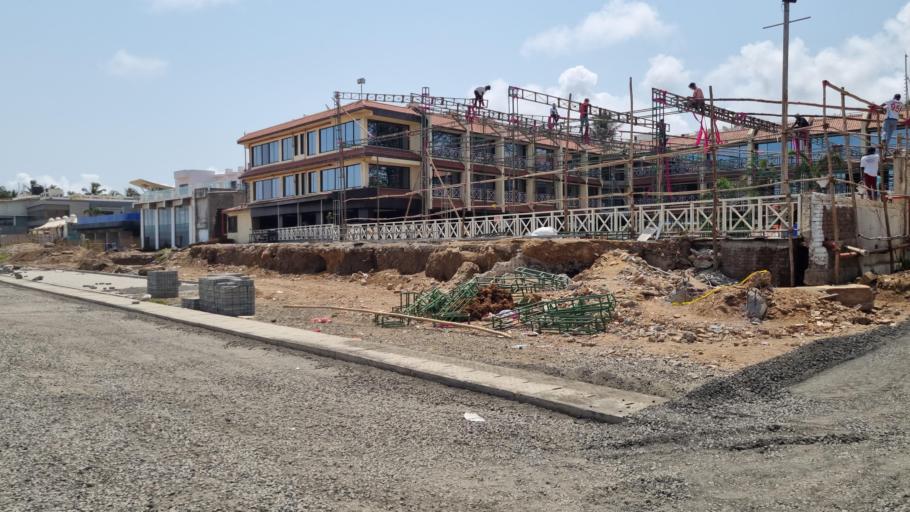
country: IN
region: Daman and Diu
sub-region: Daman District
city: Daman
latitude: 20.4476
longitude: 72.8337
